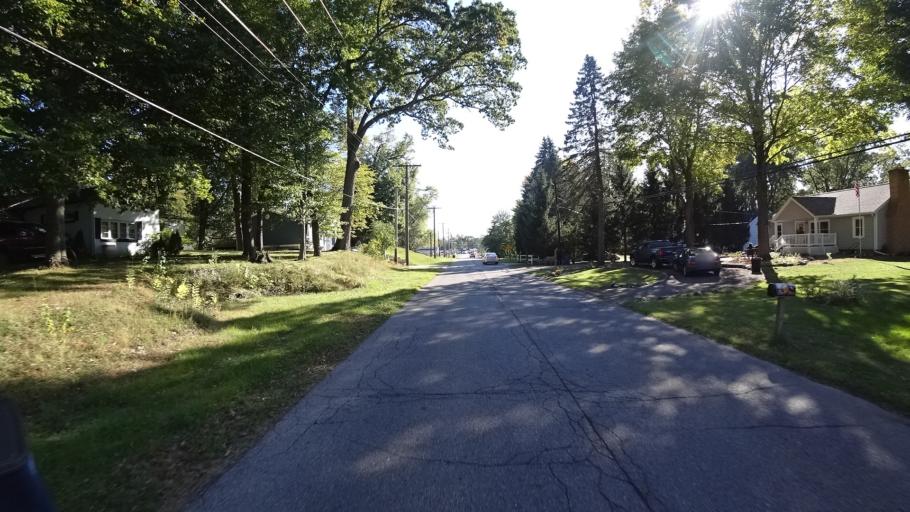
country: US
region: Indiana
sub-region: LaPorte County
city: Trail Creek
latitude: 41.7073
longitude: -86.8528
